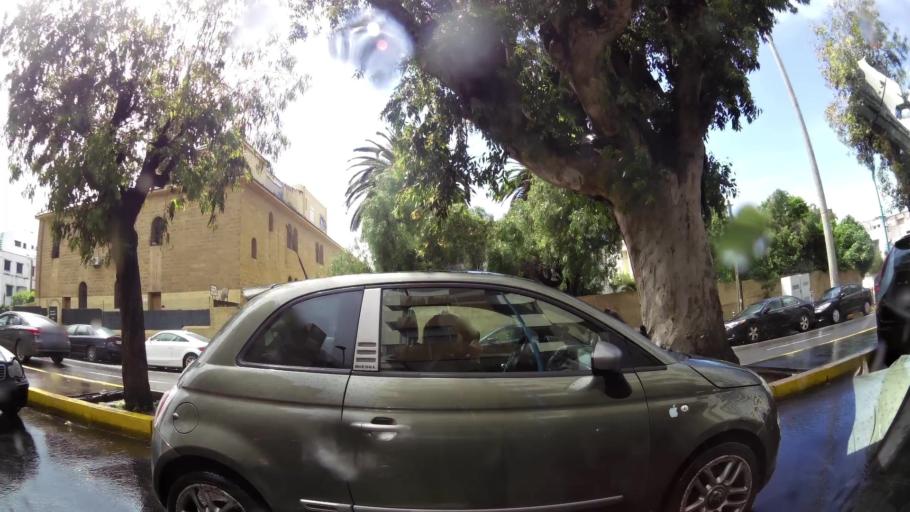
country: MA
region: Grand Casablanca
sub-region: Casablanca
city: Casablanca
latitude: 33.5719
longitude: -7.6152
